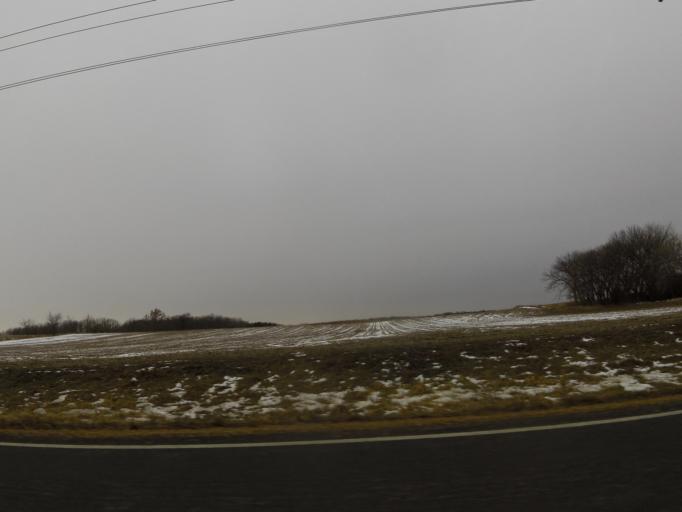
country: US
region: Minnesota
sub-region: Scott County
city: Prior Lake
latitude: 44.6751
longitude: -93.4603
